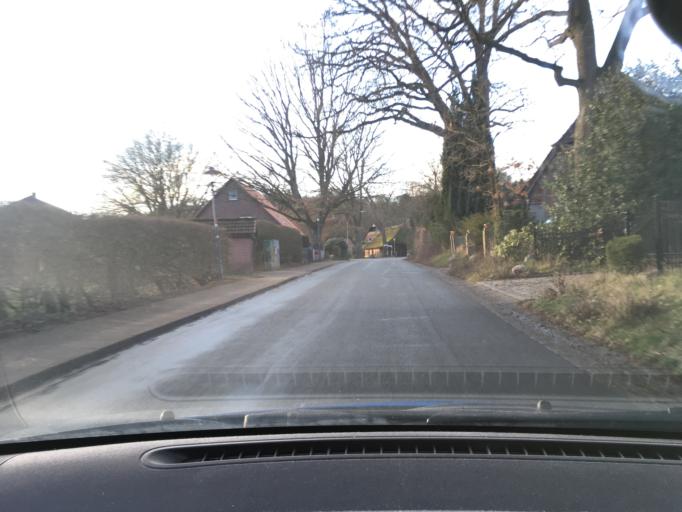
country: DE
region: Lower Saxony
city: Bendestorf
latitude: 53.3405
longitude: 9.9709
